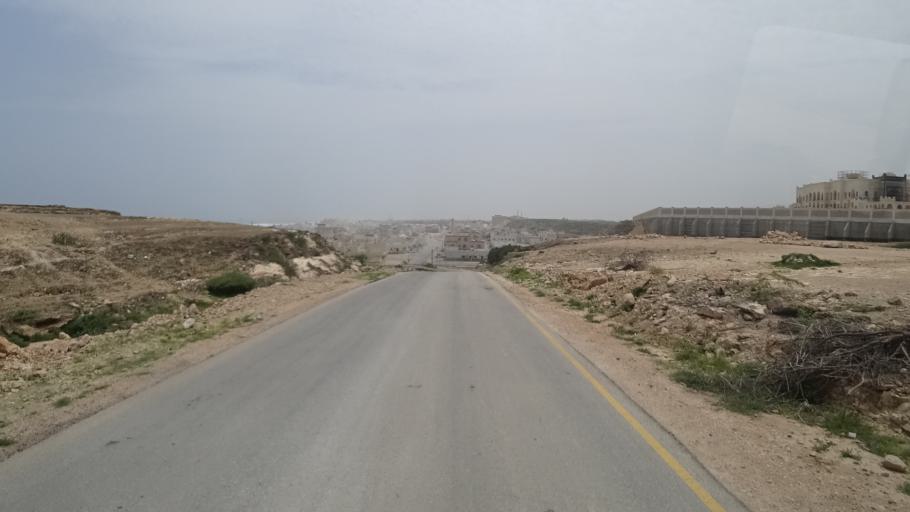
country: OM
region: Zufar
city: Salalah
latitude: 17.0371
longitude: 54.4104
